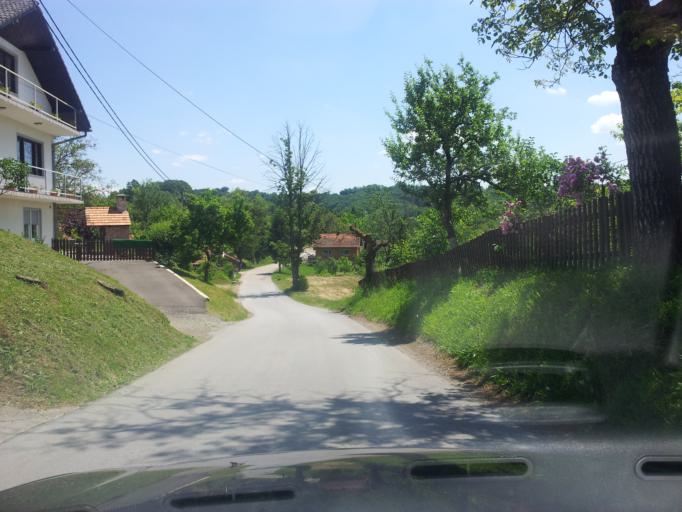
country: HR
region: Karlovacka
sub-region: Grad Karlovac
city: Karlovac
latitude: 45.4748
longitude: 15.4596
